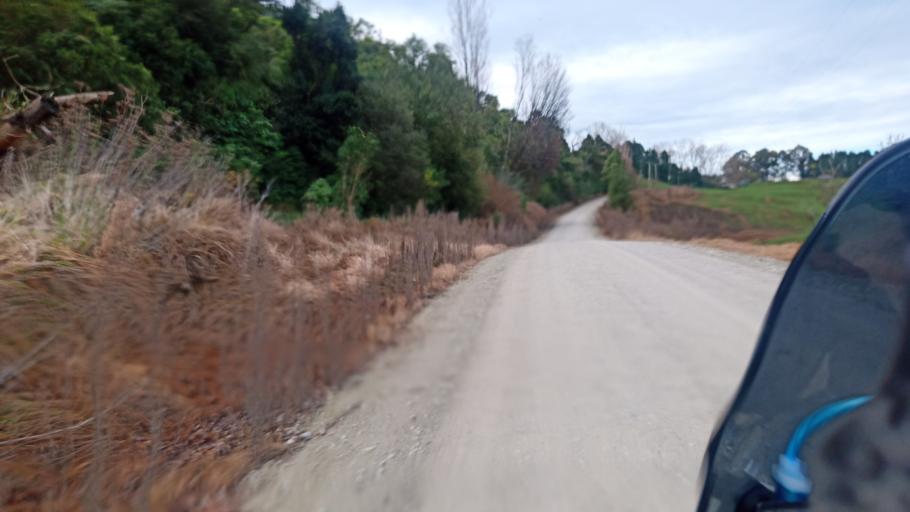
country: NZ
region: Gisborne
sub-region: Gisborne District
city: Gisborne
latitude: -38.3819
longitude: 177.9602
